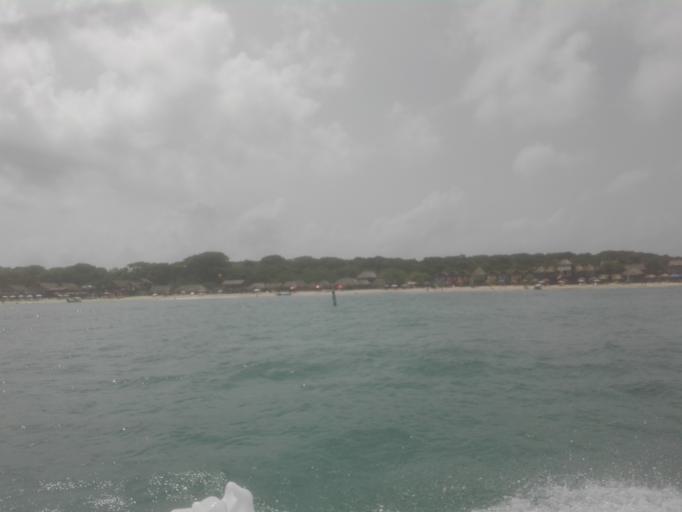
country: CO
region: Bolivar
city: Turbana
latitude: 10.2237
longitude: -75.6102
